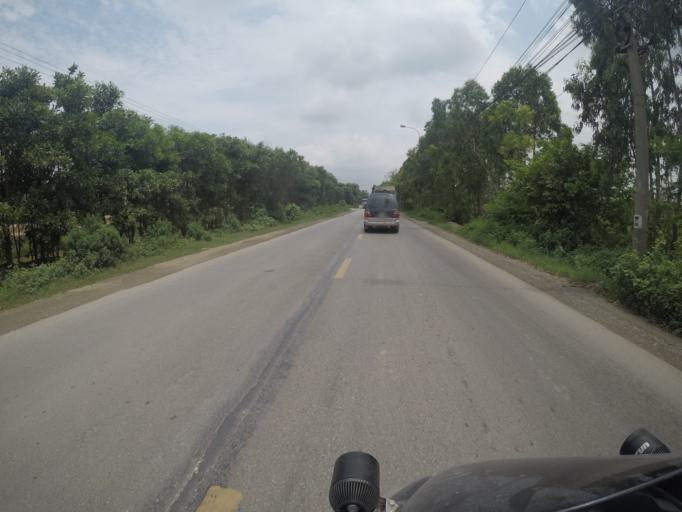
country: VN
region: Ha Noi
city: Soc Son
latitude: 21.2197
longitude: 105.8490
